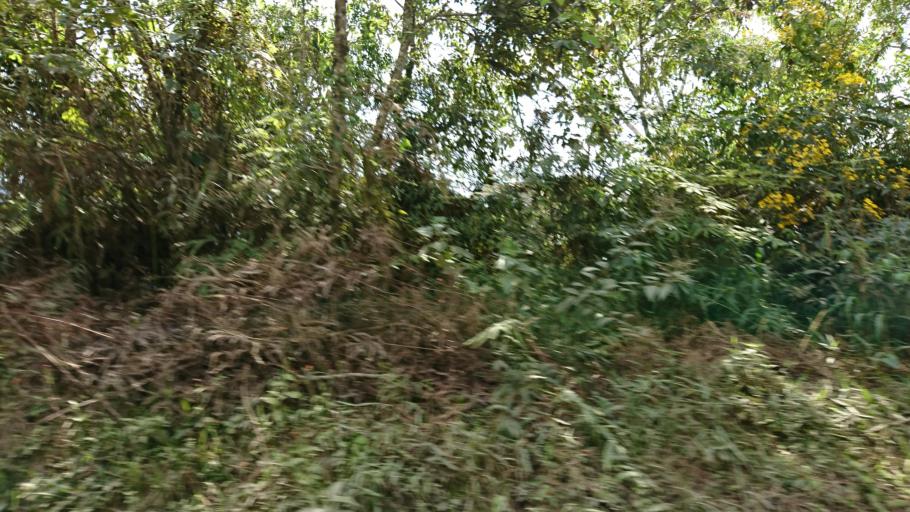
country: BO
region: La Paz
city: Coroico
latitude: -16.1286
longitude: -67.7598
